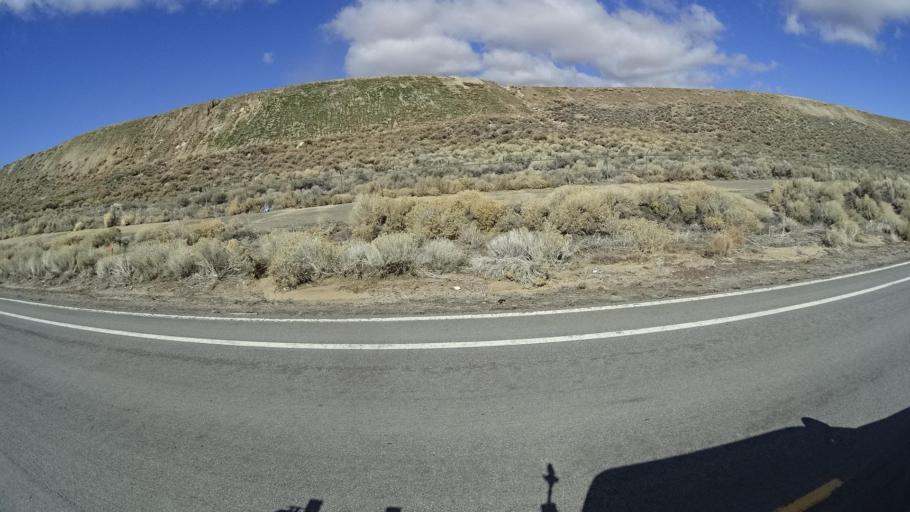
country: US
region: Nevada
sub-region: Washoe County
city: Lemmon Valley
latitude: 39.6594
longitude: -119.8639
